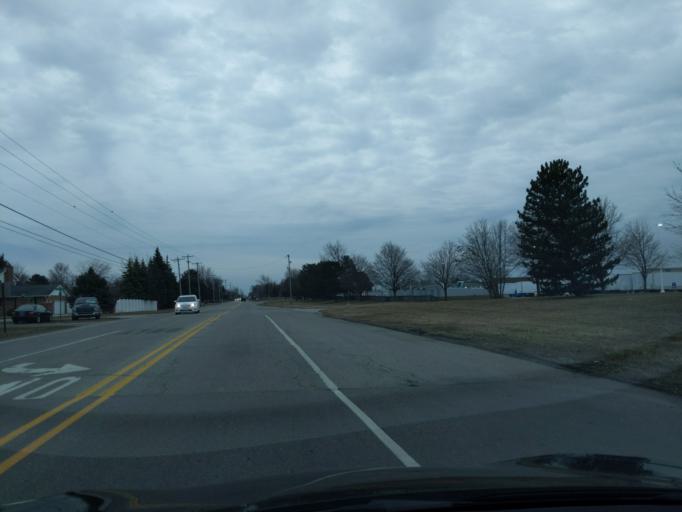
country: US
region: Michigan
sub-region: Bay County
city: Bay City
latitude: 43.6236
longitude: -83.9317
